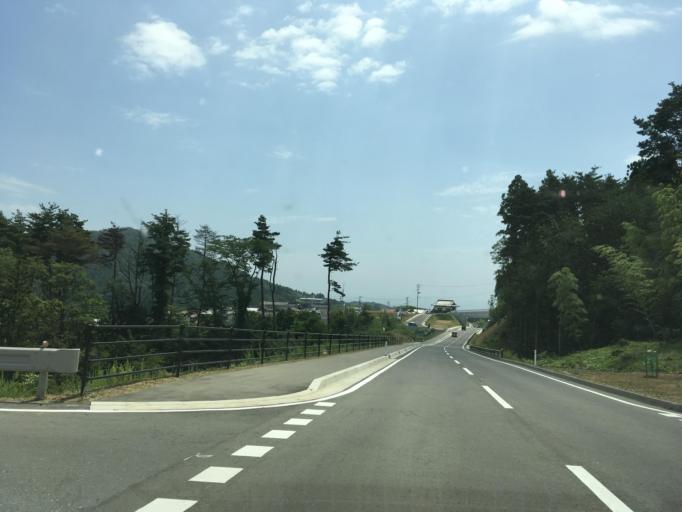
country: JP
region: Iwate
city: Ofunato
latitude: 39.0130
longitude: 141.7105
